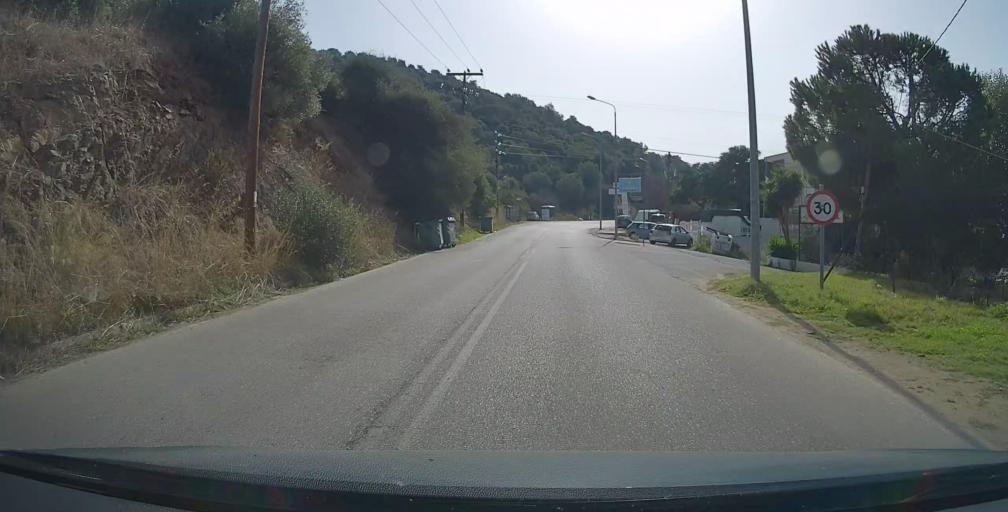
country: GR
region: Central Macedonia
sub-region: Nomos Chalkidikis
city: Sykia
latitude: 39.9721
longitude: 23.9178
